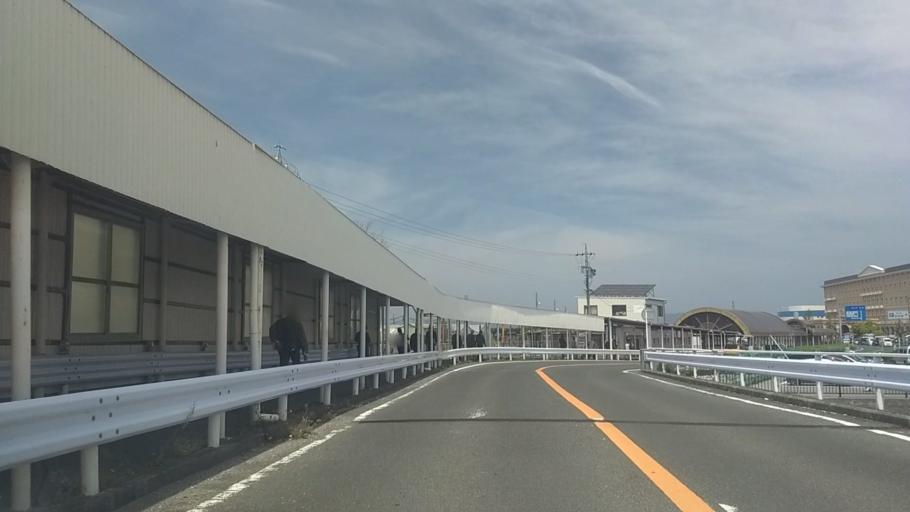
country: JP
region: Shizuoka
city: Kosai-shi
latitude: 34.6953
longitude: 137.5700
